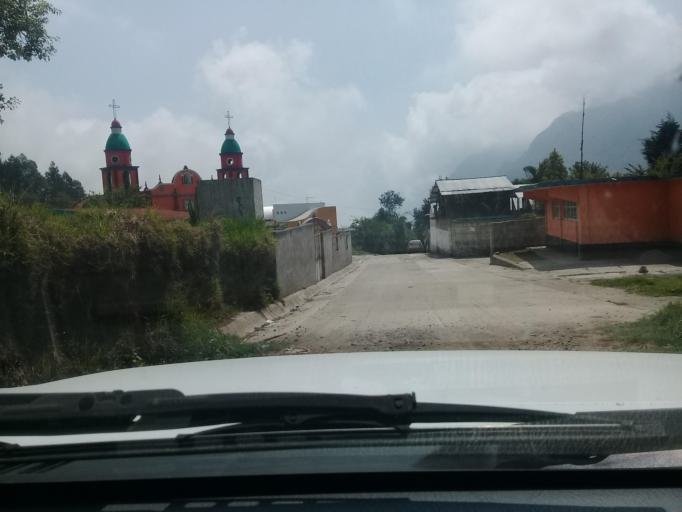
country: MX
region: Veracruz
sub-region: Mariano Escobedo
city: San Isidro el Berro
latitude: 18.9460
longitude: -97.2101
